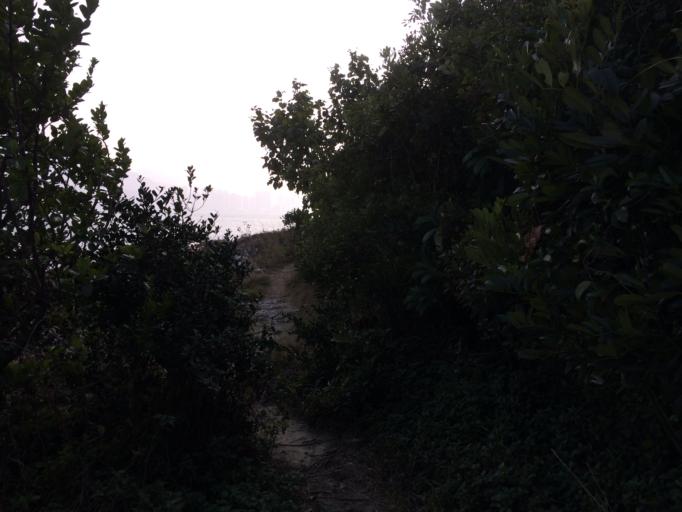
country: HK
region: Tai Po
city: Tai Po
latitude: 22.4555
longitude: 114.2336
